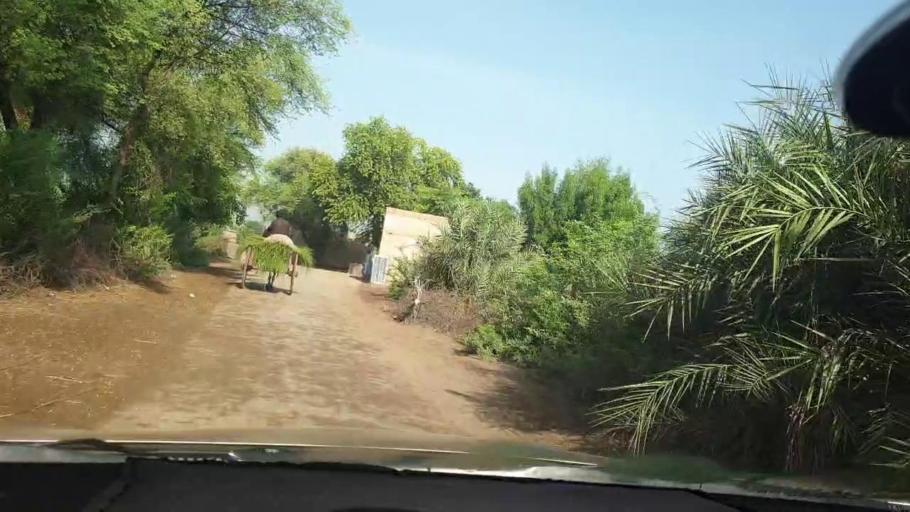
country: PK
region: Sindh
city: Kambar
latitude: 27.6602
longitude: 68.0171
